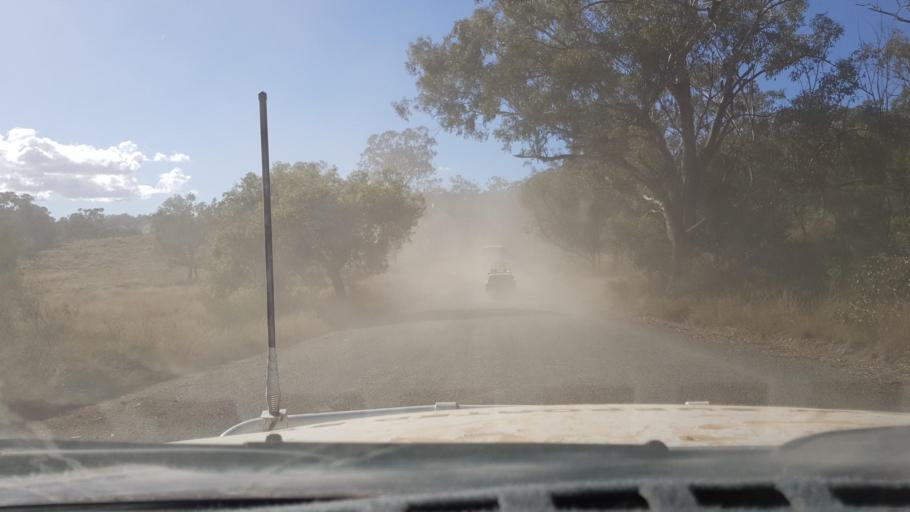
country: AU
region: New South Wales
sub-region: Tamworth Municipality
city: Manilla
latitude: -30.6592
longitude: 150.4754
